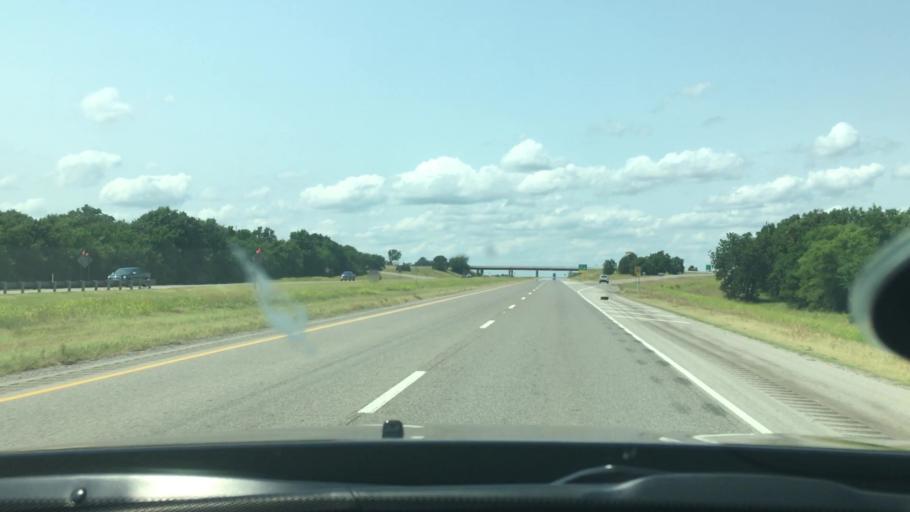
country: US
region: Oklahoma
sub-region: Murray County
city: Davis
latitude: 34.5015
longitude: -97.1707
